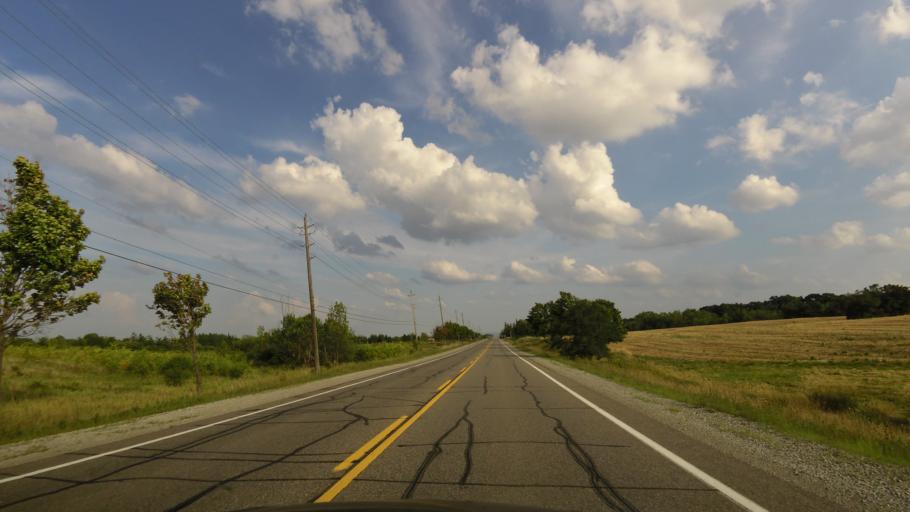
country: CA
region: Ontario
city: Burlington
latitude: 43.3826
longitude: -79.8464
